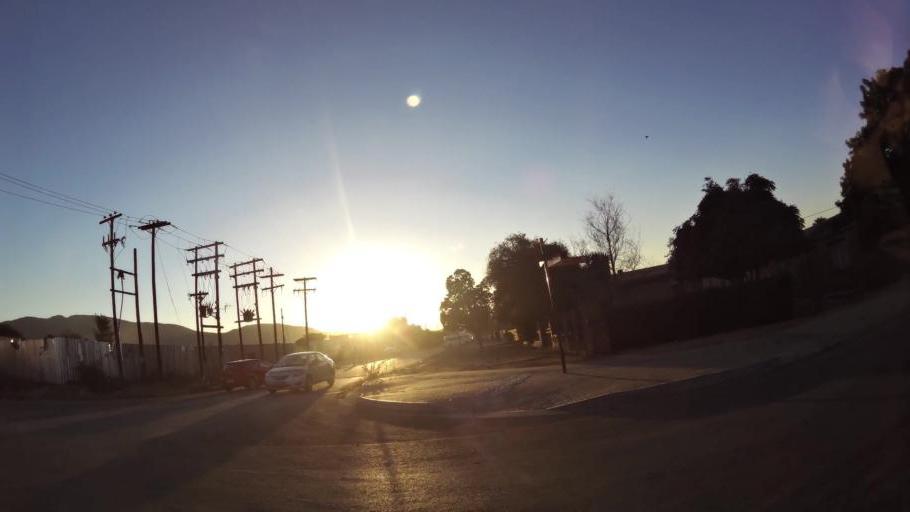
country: ZA
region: North-West
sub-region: Bojanala Platinum District Municipality
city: Rustenburg
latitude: -25.6468
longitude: 27.2158
